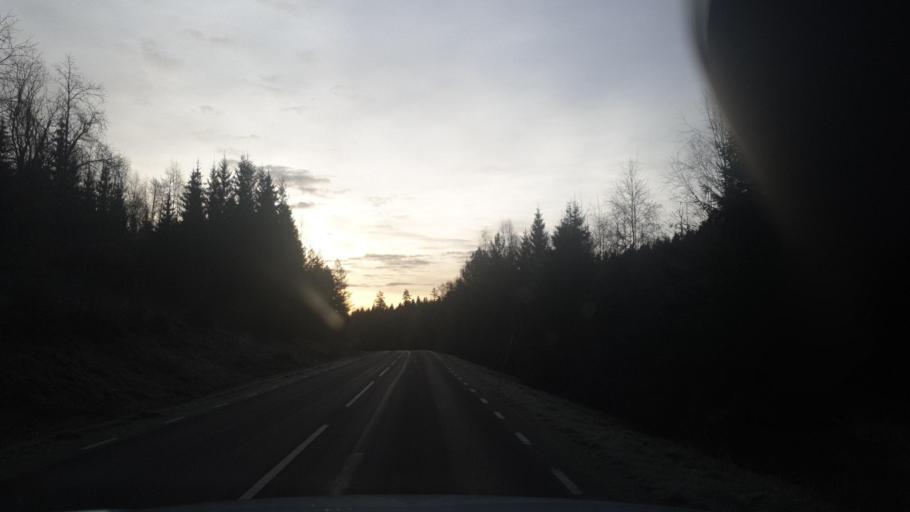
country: SE
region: Vaermland
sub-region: Grums Kommun
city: Slottsbron
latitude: 59.4567
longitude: 12.8375
